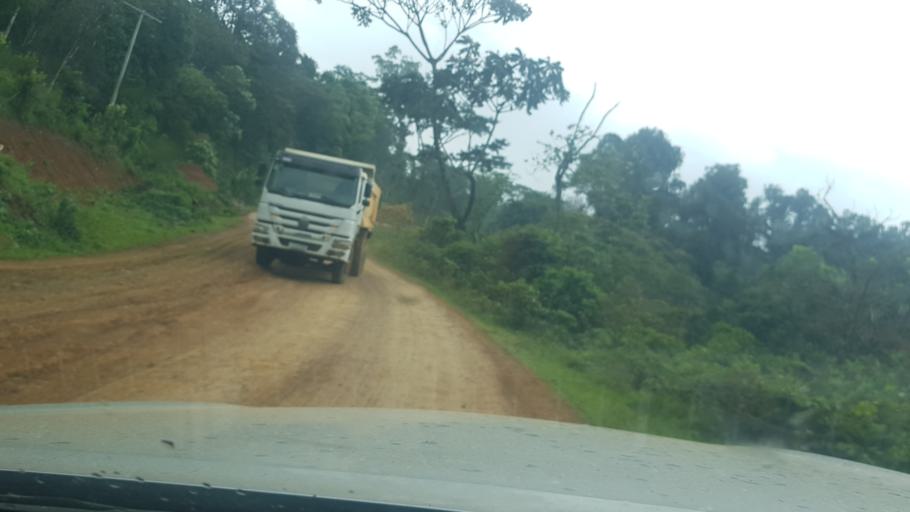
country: ET
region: Oromiya
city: Gore
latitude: 7.8787
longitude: 35.4846
